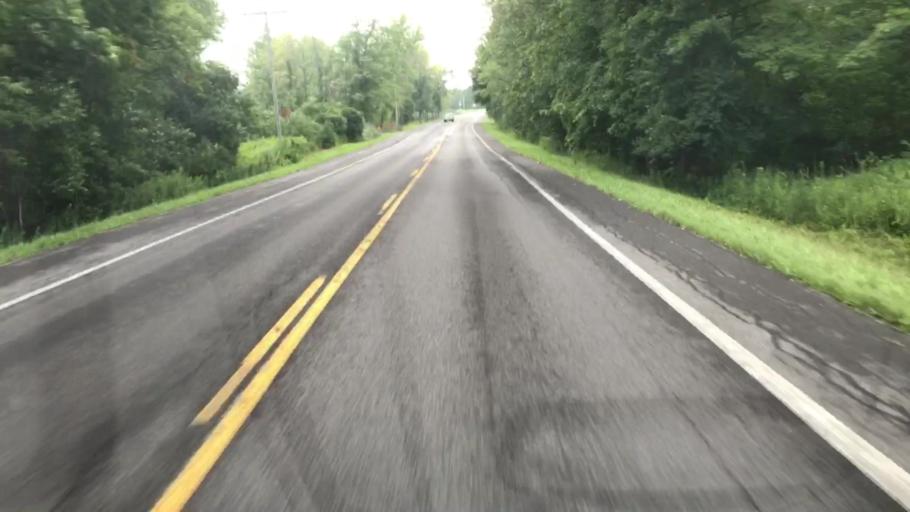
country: US
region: New York
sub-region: Onondaga County
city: Liverpool
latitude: 43.1552
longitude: -76.1915
